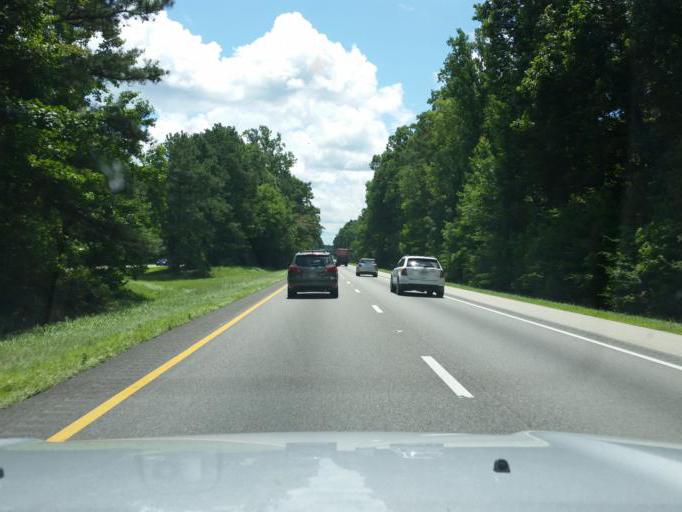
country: US
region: Virginia
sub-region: City of Williamsburg
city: Williamsburg
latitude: 37.3319
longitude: -76.7082
